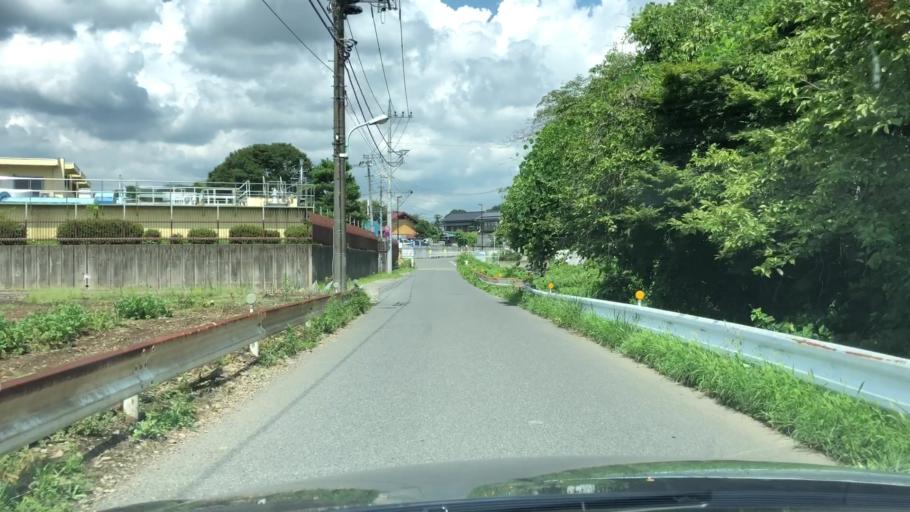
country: JP
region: Tokyo
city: Fussa
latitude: 35.7187
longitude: 139.2800
